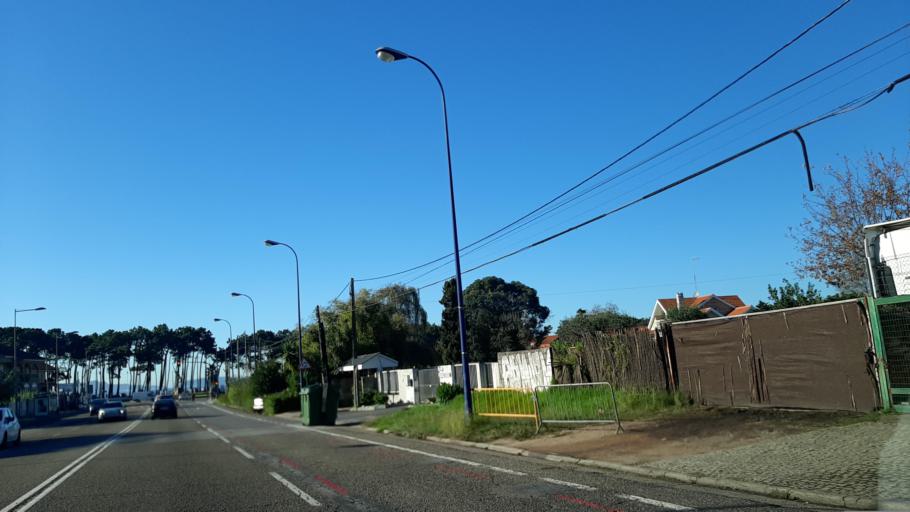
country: ES
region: Galicia
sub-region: Provincia de Pontevedra
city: Vigo
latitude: 42.2111
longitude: -8.7719
